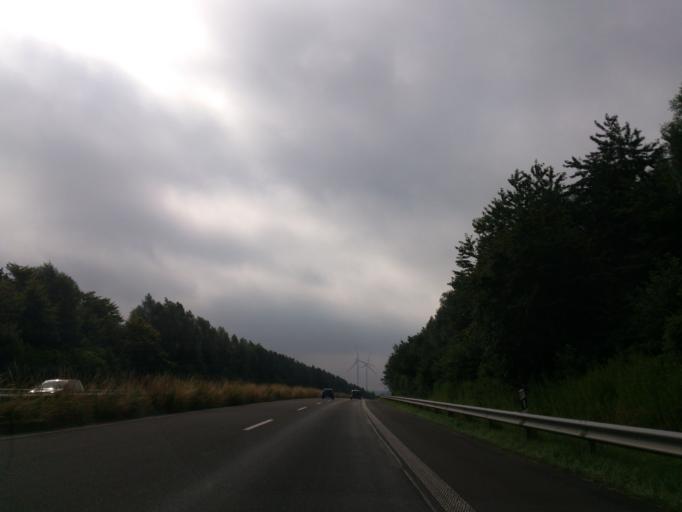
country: DE
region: Schleswig-Holstein
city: Arkebek
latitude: 54.1542
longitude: 9.2329
